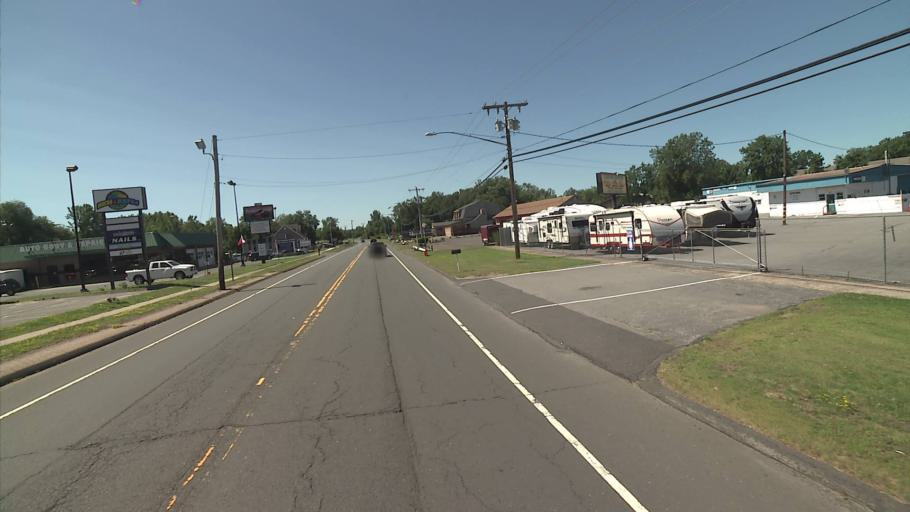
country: US
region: Connecticut
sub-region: Hartford County
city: Plainville
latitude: 41.6478
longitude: -72.8722
